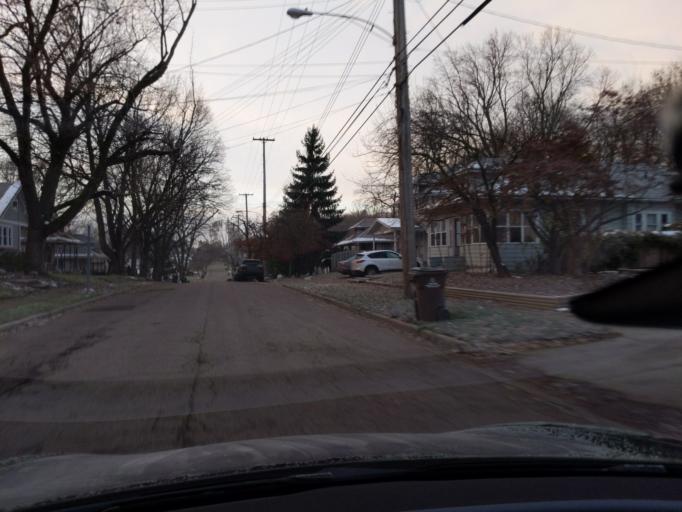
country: US
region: Michigan
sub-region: Ingham County
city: Lansing
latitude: 42.7097
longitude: -84.5522
